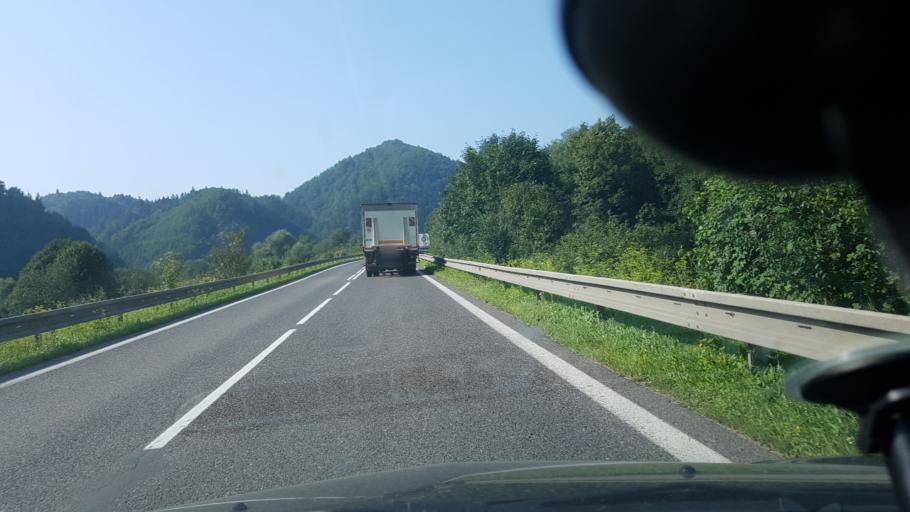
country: SK
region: Zilinsky
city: Tvrdosin
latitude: 49.2727
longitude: 19.4618
